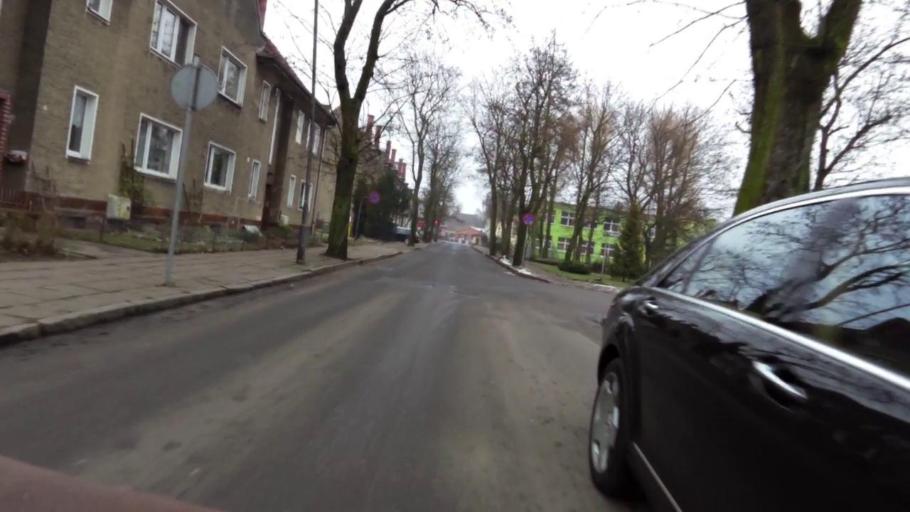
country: PL
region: West Pomeranian Voivodeship
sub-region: Powiat walecki
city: Walcz
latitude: 53.2772
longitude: 16.4815
